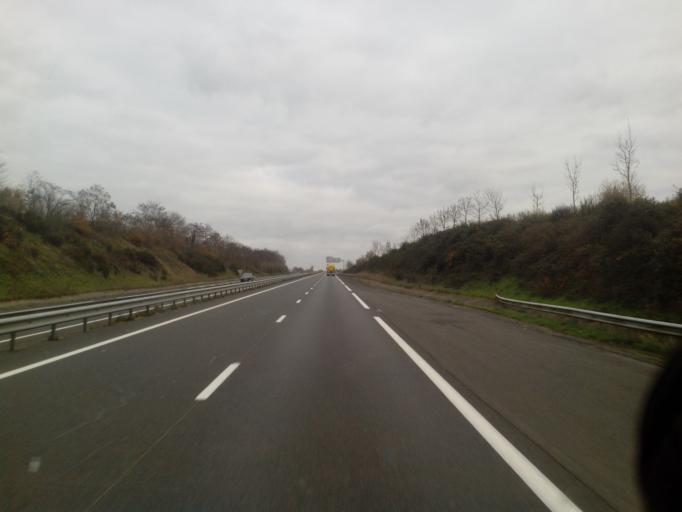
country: FR
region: Poitou-Charentes
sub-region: Departement des Deux-Sevres
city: Bressuire
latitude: 46.8558
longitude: -0.4866
